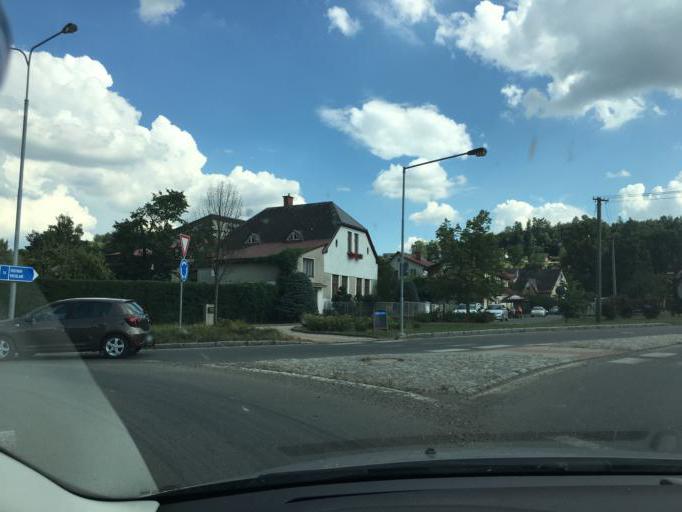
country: CZ
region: Liberecky
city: Jilemnice
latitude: 50.6219
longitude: 15.5073
